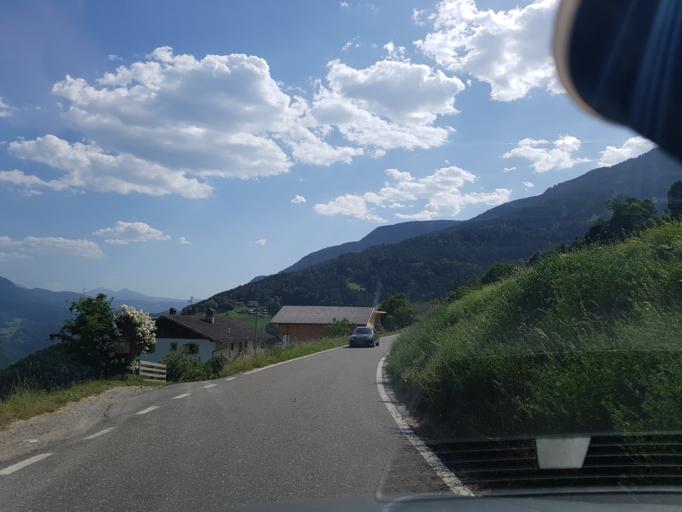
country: IT
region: Trentino-Alto Adige
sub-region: Bolzano
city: Villandro - Villanders
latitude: 46.6252
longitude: 11.5299
